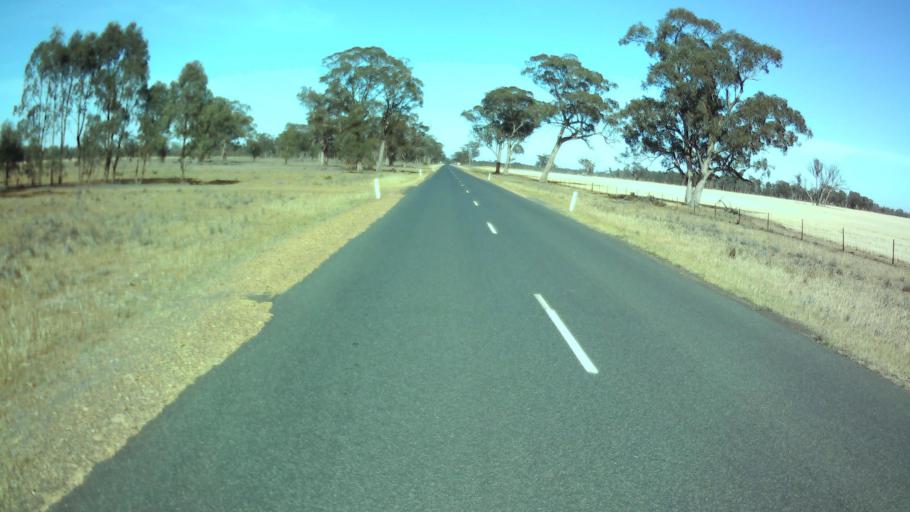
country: AU
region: New South Wales
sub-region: Weddin
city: Grenfell
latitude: -34.1365
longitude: 147.7679
